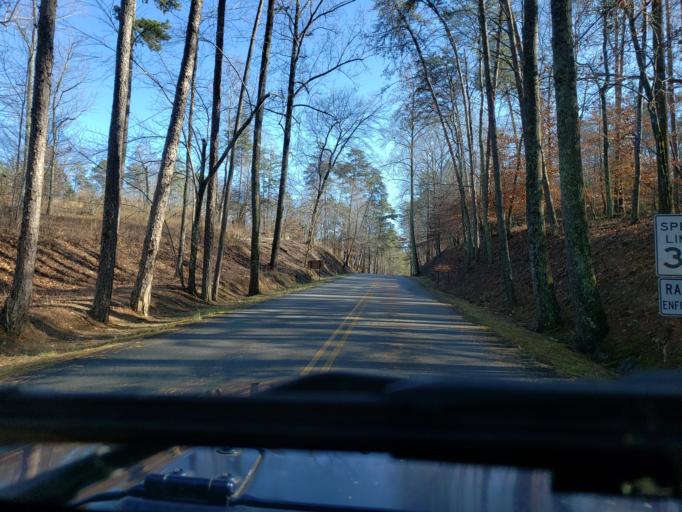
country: US
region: North Carolina
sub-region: Cleveland County
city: White Plains
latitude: 35.1522
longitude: -81.3948
